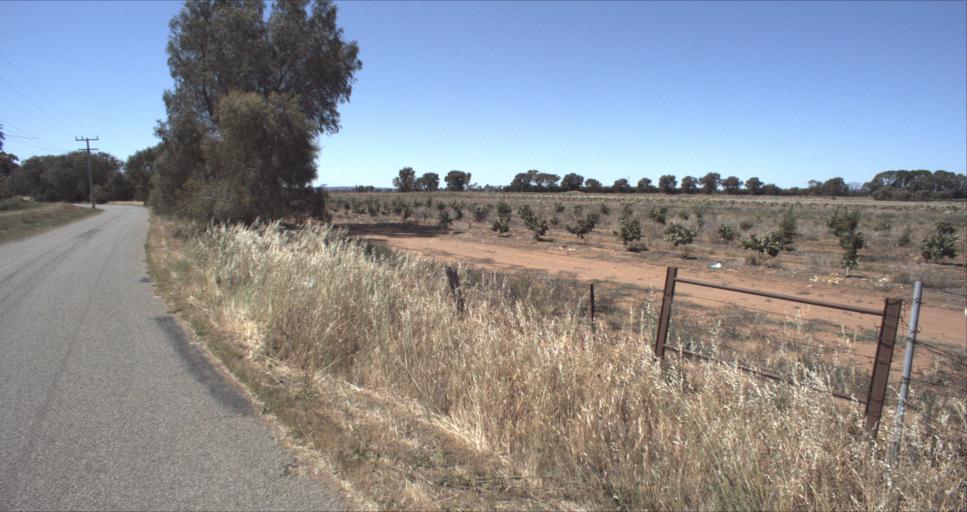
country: AU
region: New South Wales
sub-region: Leeton
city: Leeton
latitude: -34.5277
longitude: 146.3459
